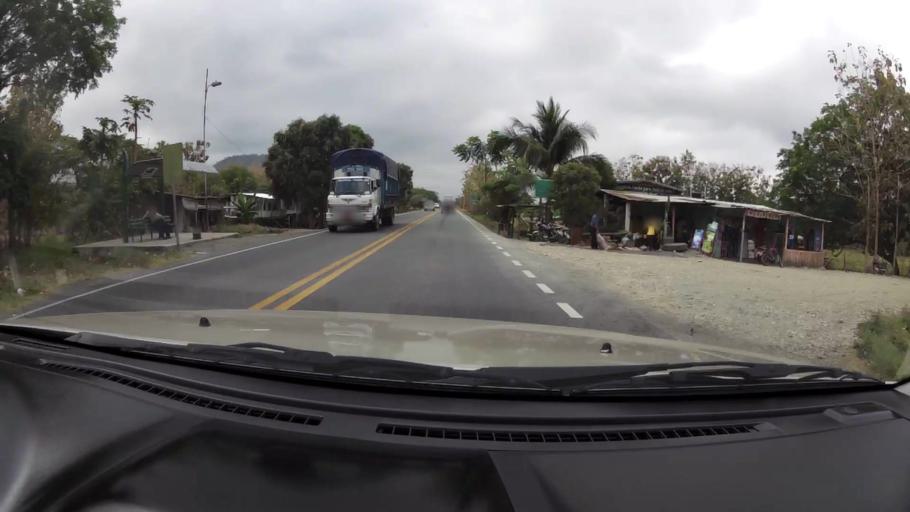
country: EC
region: Guayas
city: Naranjal
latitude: -2.4196
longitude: -79.6247
